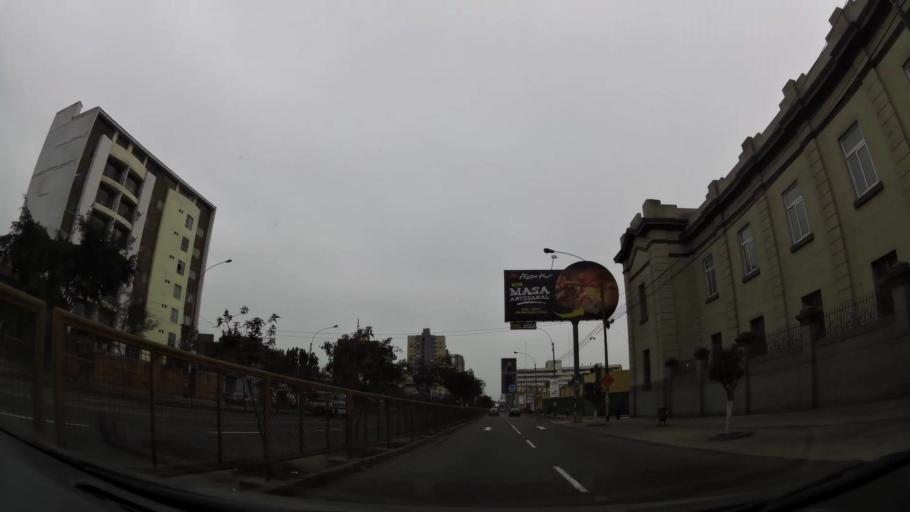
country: PE
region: Lima
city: Lima
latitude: -12.0631
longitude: -77.0441
